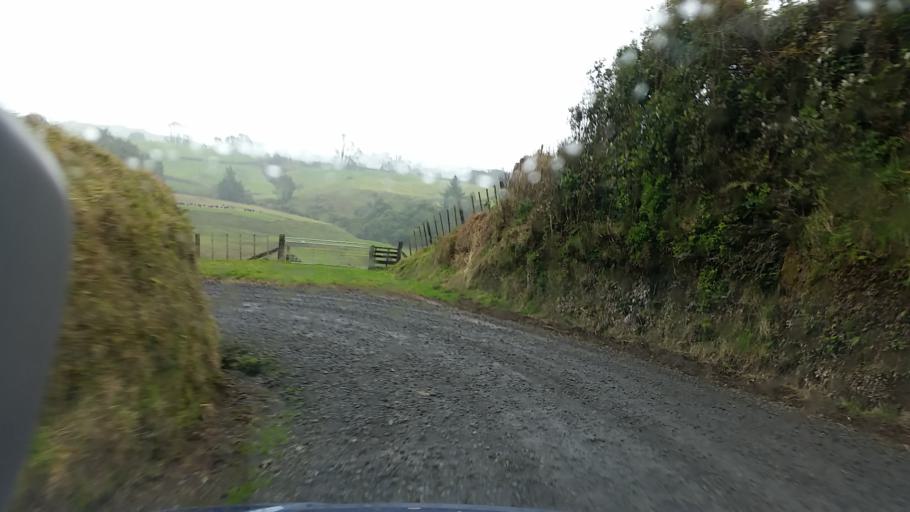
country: NZ
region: Taranaki
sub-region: South Taranaki District
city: Eltham
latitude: -39.2769
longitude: 174.3383
